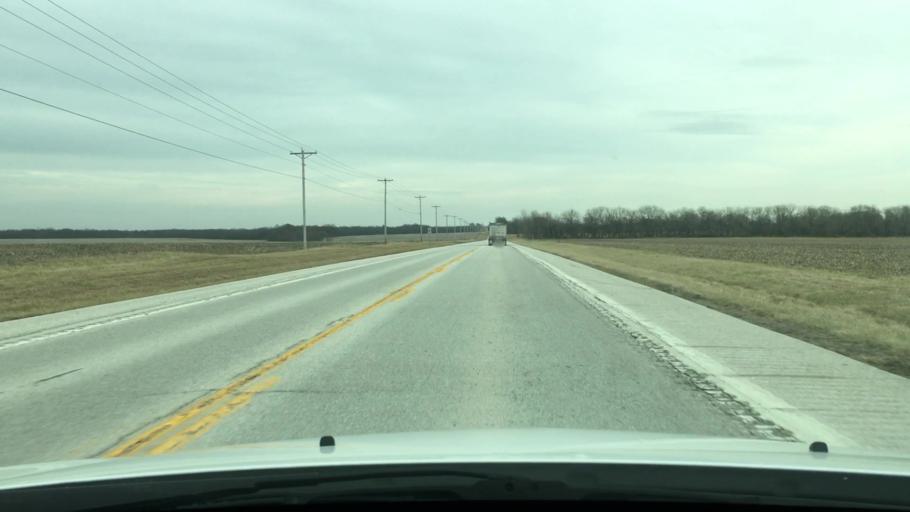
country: US
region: Missouri
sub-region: Pike County
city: Bowling Green
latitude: 39.3445
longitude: -91.2948
